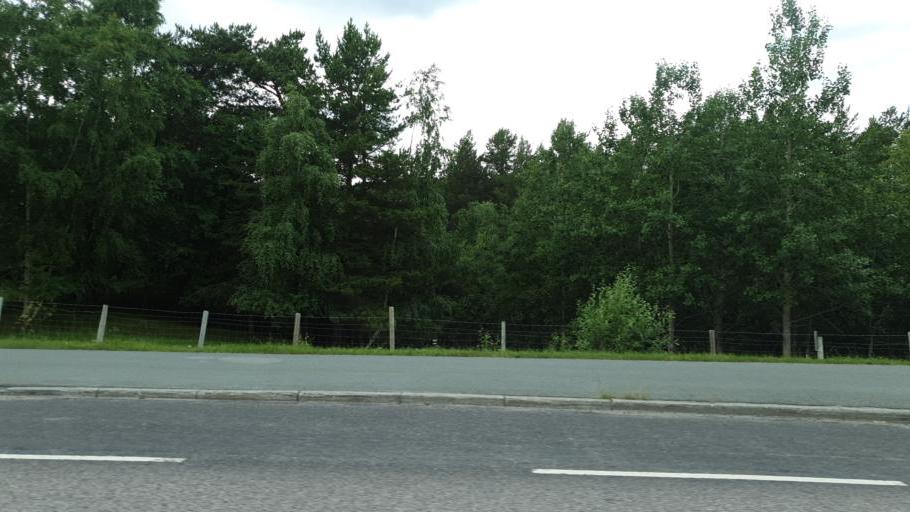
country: NO
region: Sor-Trondelag
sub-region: Oppdal
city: Oppdal
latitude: 62.5704
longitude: 9.6472
